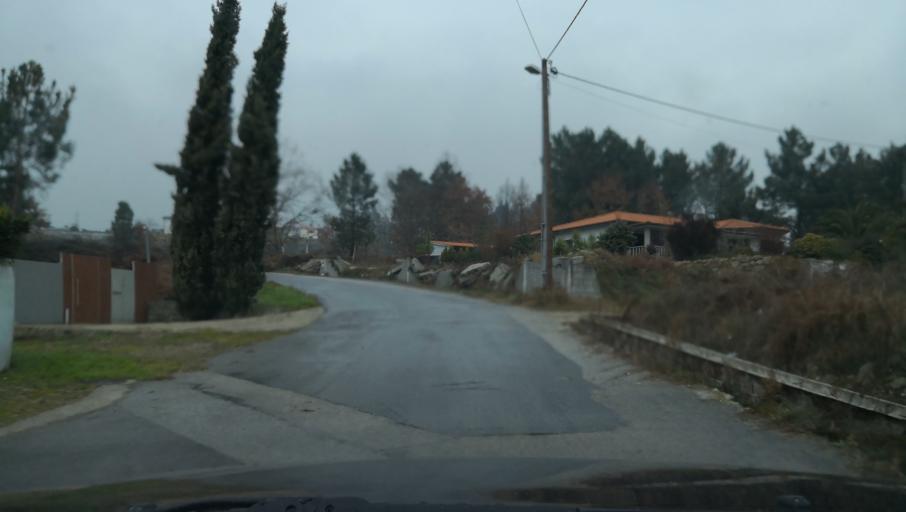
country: PT
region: Vila Real
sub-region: Vila Real
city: Vila Real
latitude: 41.3019
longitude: -7.7803
